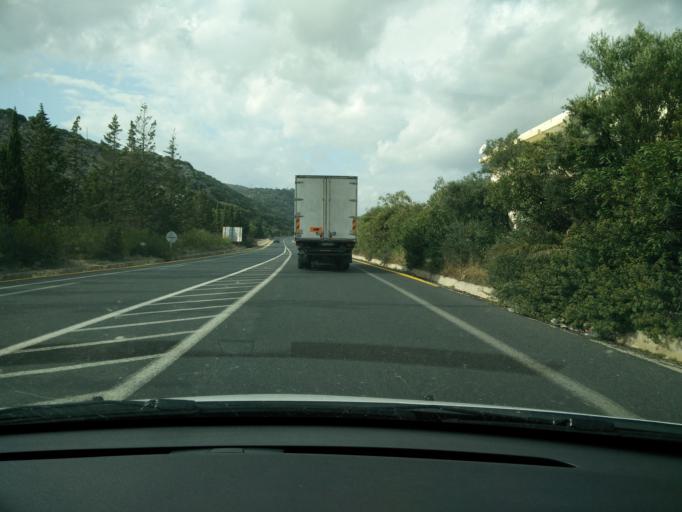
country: GR
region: Crete
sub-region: Nomos Lasithiou
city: Agios Nikolaos
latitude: 35.2008
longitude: 25.7044
